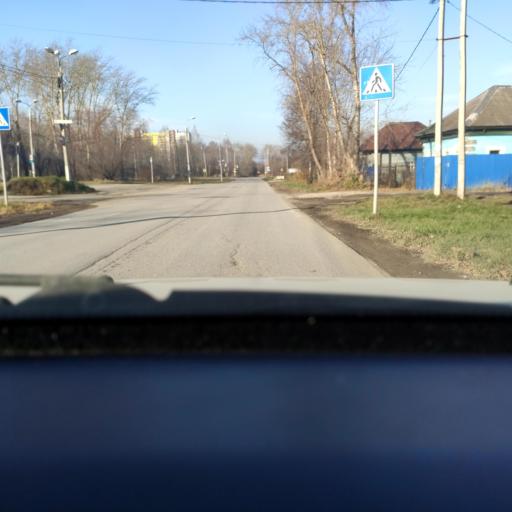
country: RU
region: Perm
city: Perm
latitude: 58.0916
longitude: 56.3858
